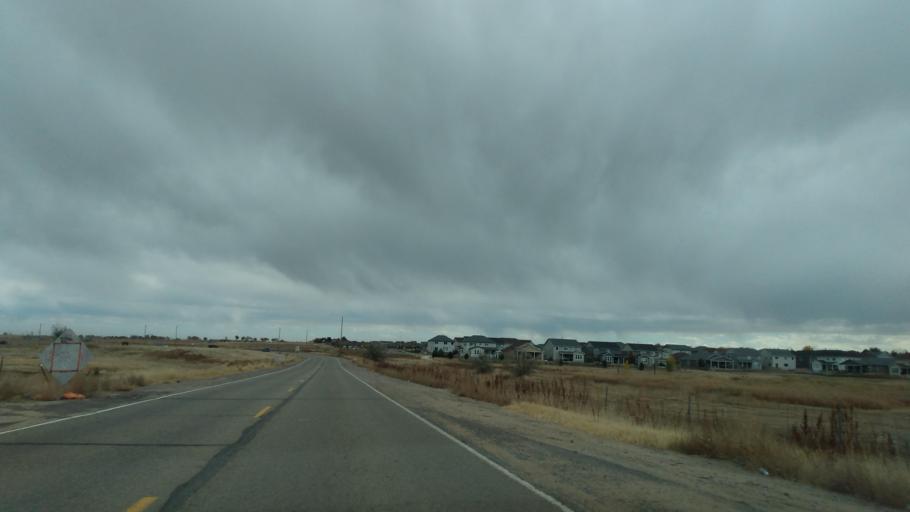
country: US
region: Colorado
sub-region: Adams County
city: Northglenn
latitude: 39.9726
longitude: -104.9648
